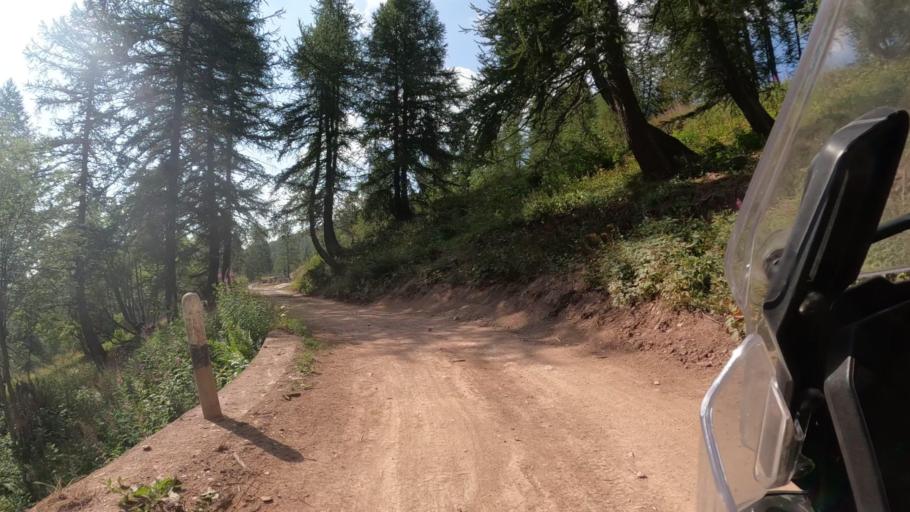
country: IT
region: Piedmont
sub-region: Provincia di Cuneo
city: Briga Alta
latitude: 44.1174
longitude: 7.6977
